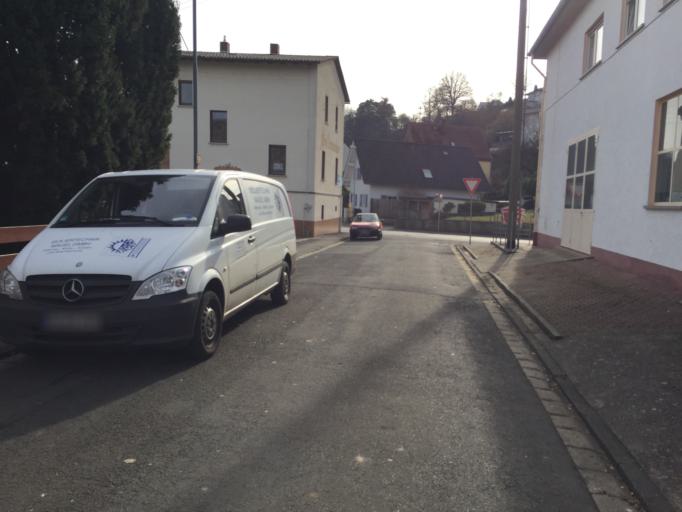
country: DE
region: Hesse
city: Lollar
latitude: 50.6728
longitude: 8.7061
